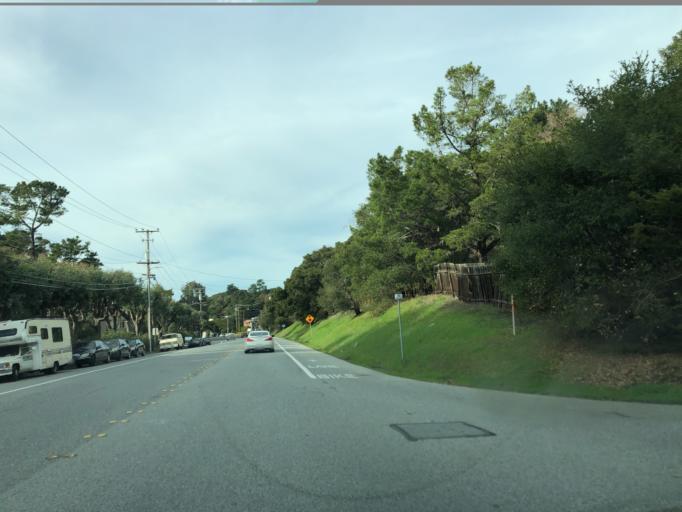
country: US
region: California
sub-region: San Mateo County
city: Highlands-Baywood Park
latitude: 37.5180
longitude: -122.3361
